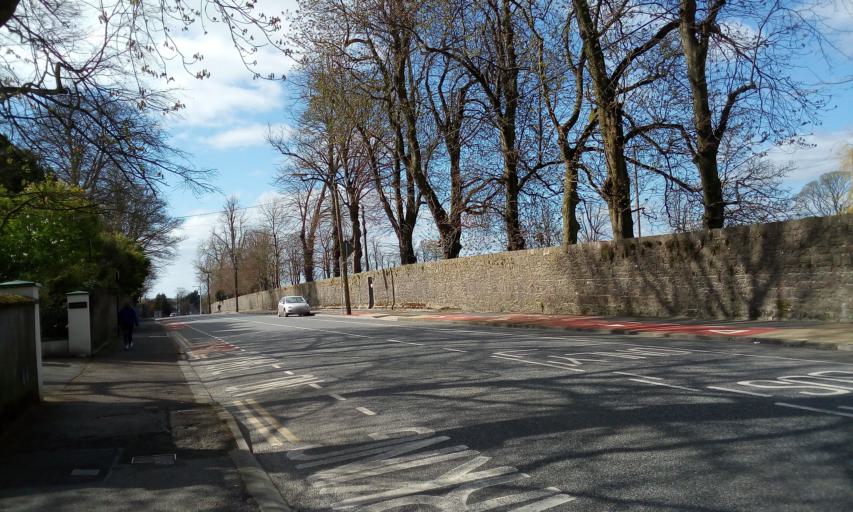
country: IE
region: Leinster
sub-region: Kilkenny
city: Kilkenny
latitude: 52.6464
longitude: -7.2546
